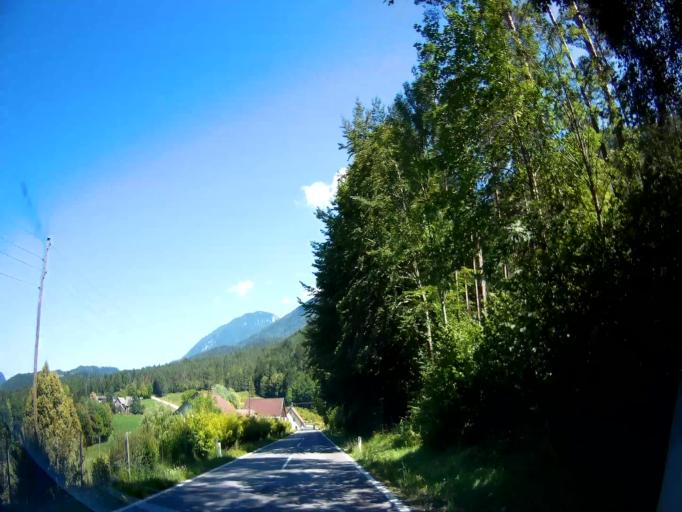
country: AT
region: Carinthia
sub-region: Politischer Bezirk Klagenfurt Land
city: Ebenthal
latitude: 46.5385
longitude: 14.3788
